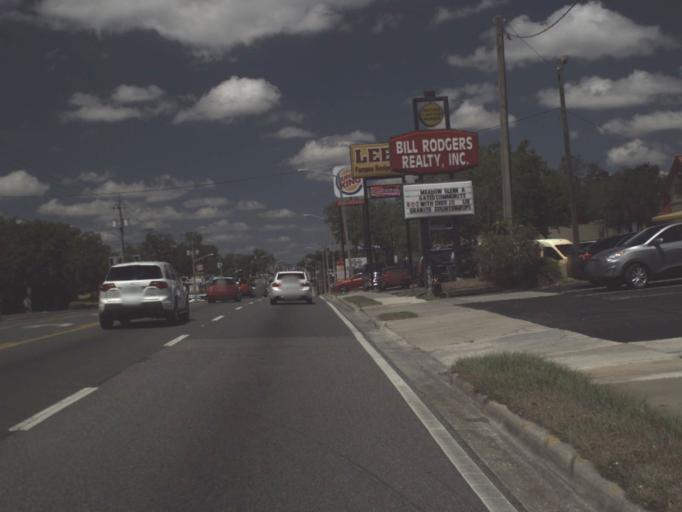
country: US
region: Florida
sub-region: Marion County
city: Ocala
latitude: 29.1869
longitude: -82.1052
